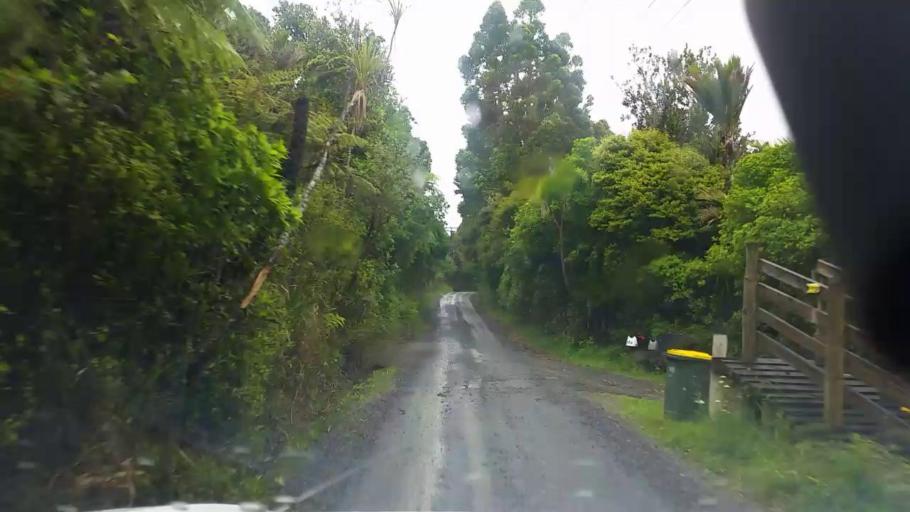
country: NZ
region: Auckland
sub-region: Auckland
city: Muriwai Beach
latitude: -36.8433
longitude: 174.4923
